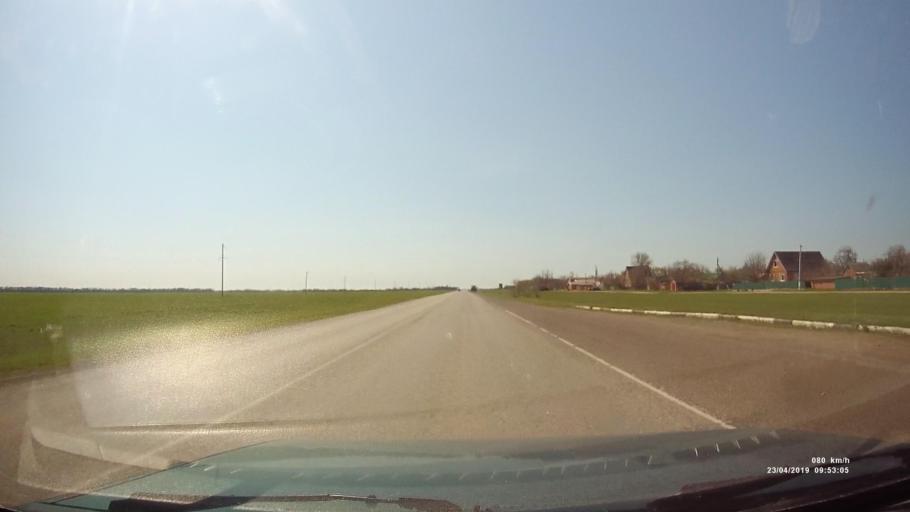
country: RU
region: Rostov
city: Orlovskiy
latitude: 46.8371
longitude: 42.0486
